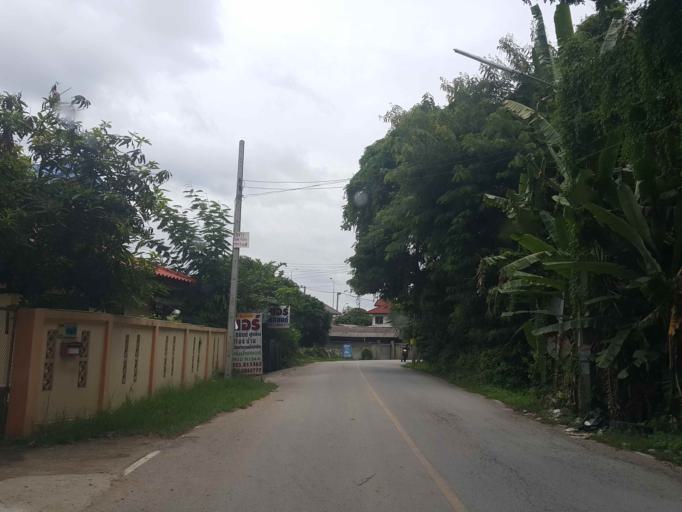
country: TH
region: Chiang Mai
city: Chiang Mai
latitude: 18.7476
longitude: 98.9843
